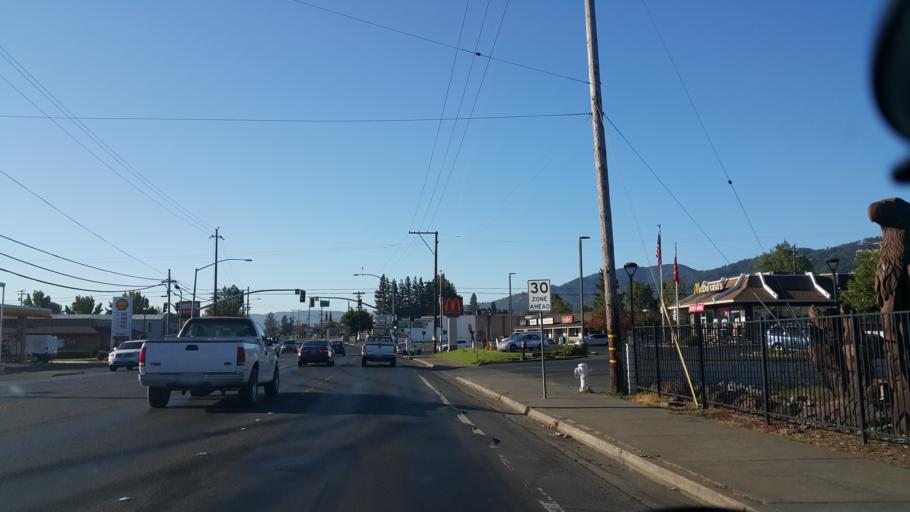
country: US
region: California
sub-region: Mendocino County
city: Ukiah
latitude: 39.1685
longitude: -123.2114
